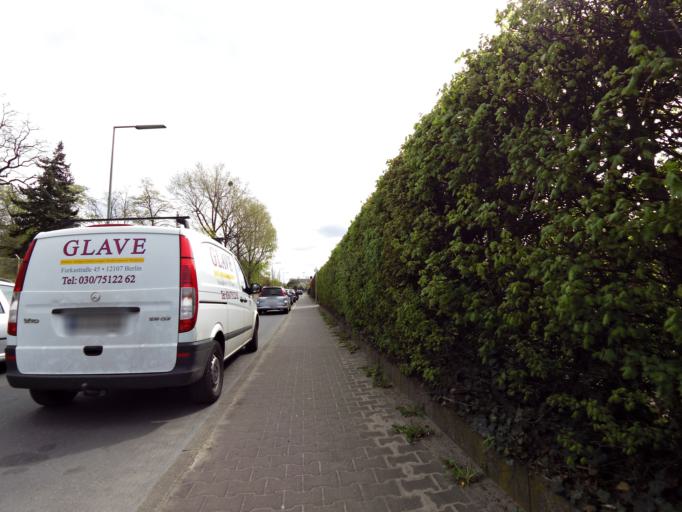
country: DE
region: Berlin
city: Tempelhof Bezirk
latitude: 52.4519
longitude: 13.4122
